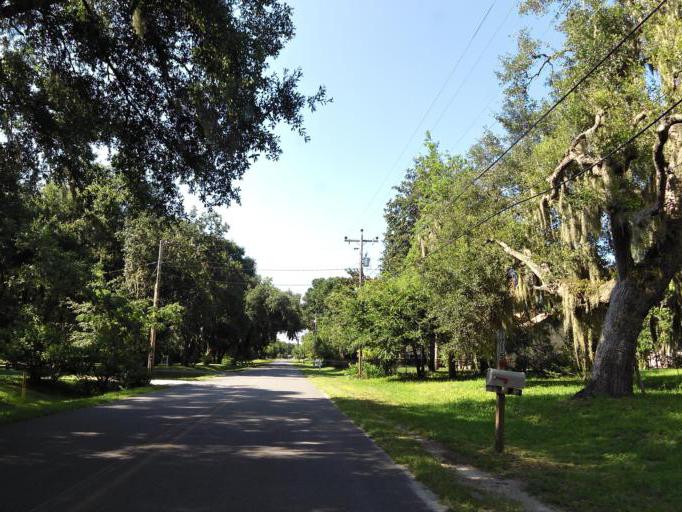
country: US
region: Florida
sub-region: Nassau County
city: Fernandina Beach
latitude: 30.6470
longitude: -81.4628
